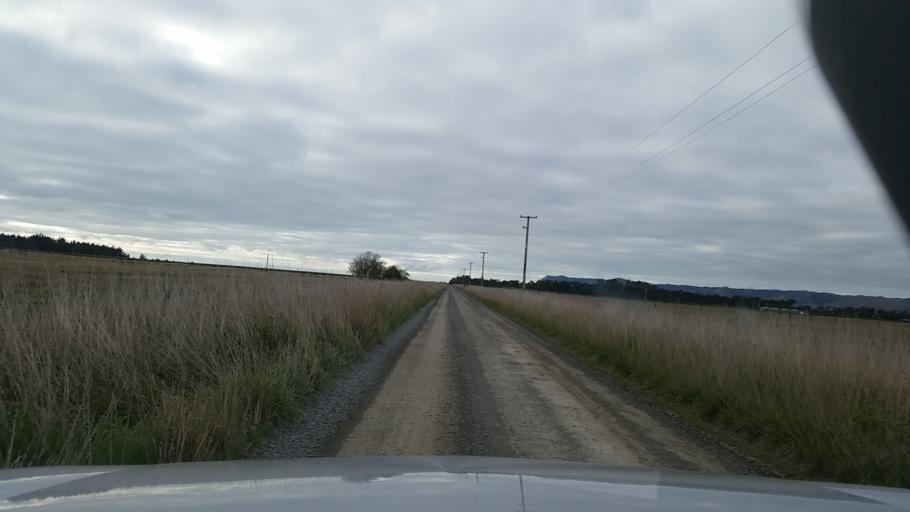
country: NZ
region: Marlborough
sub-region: Marlborough District
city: Blenheim
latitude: -41.5091
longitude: 174.0306
